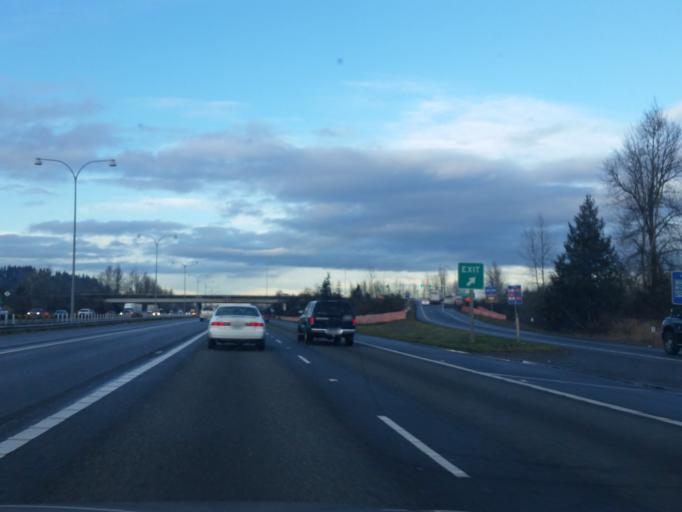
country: US
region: Washington
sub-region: King County
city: Auburn
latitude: 47.3198
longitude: -122.2448
